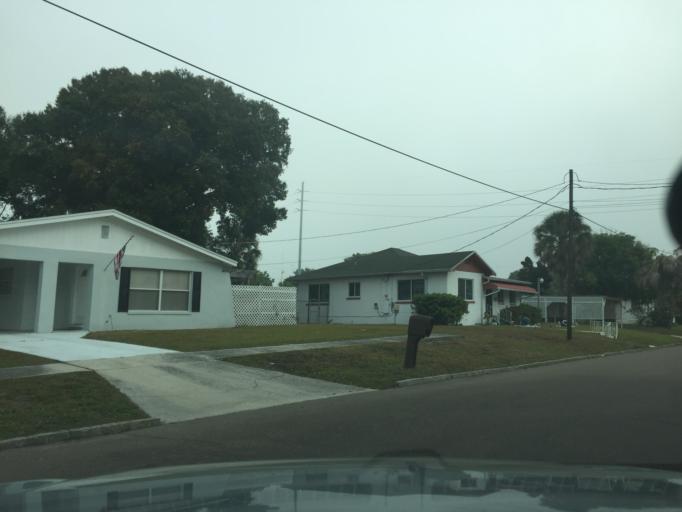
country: US
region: Florida
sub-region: Hillsborough County
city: Tampa
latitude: 27.9543
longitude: -82.4871
